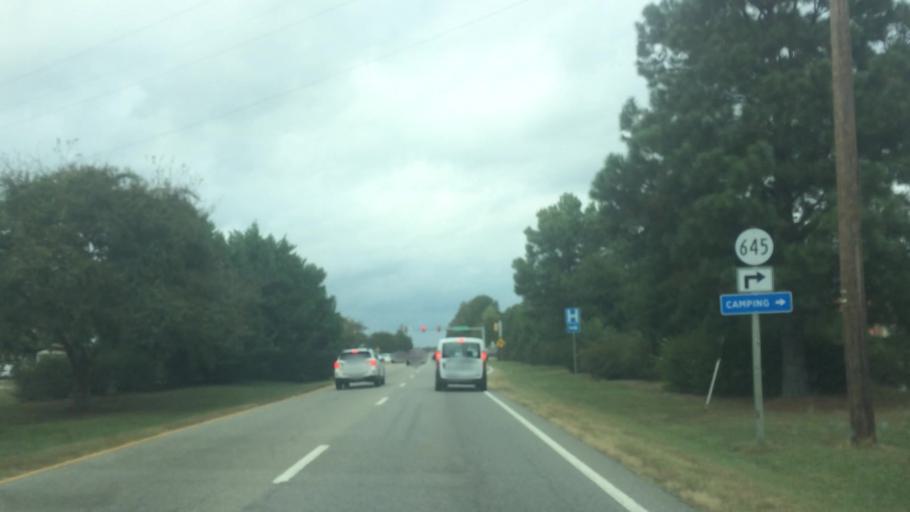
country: US
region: Virginia
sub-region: James City County
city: Williamsburg
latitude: 37.3114
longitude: -76.7315
